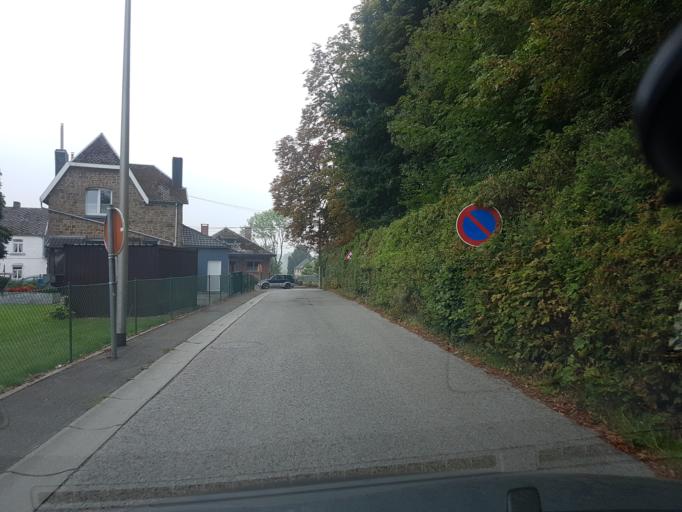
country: BE
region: Wallonia
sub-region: Province de Namur
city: Ohey
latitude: 50.4354
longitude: 5.1184
